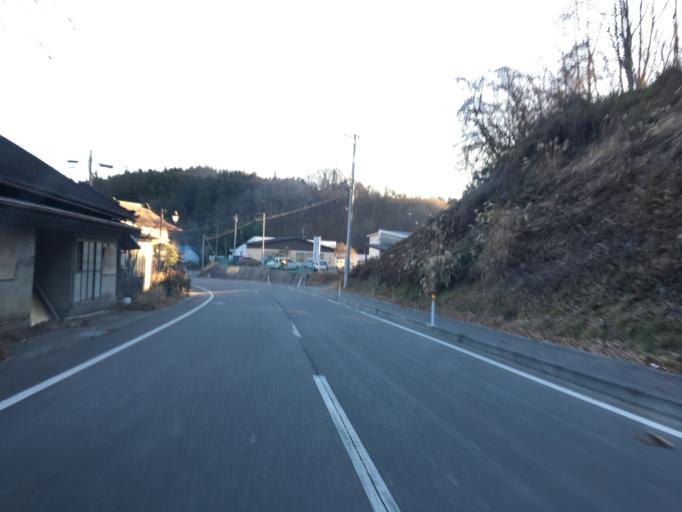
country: JP
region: Fukushima
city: Ishikawa
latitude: 37.1878
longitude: 140.5631
